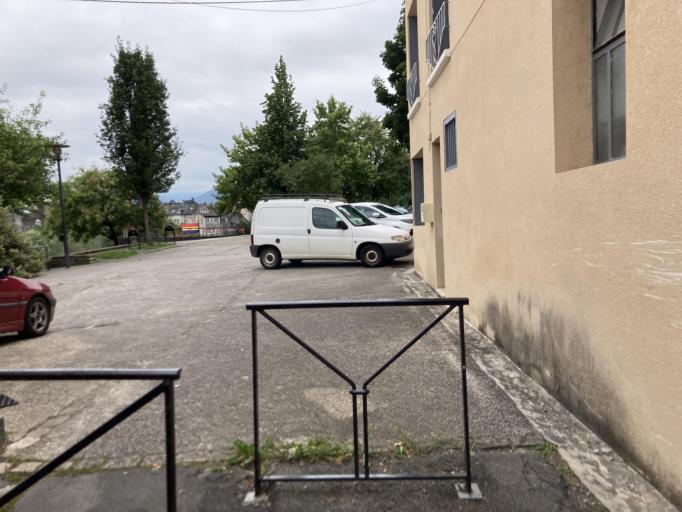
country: FR
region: Aquitaine
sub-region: Departement des Pyrenees-Atlantiques
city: Oloron-Sainte-Marie
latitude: 43.1913
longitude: -0.6095
